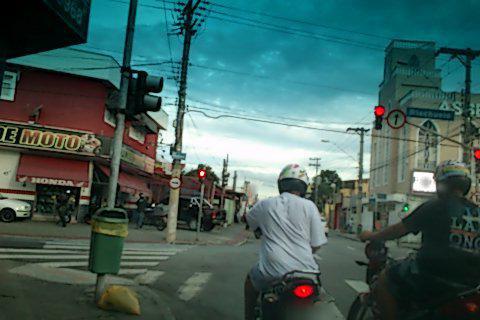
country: BR
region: Sao Paulo
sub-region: Sao Jose Dos Campos
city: Sao Jose dos Campos
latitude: -23.1913
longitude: -45.8768
